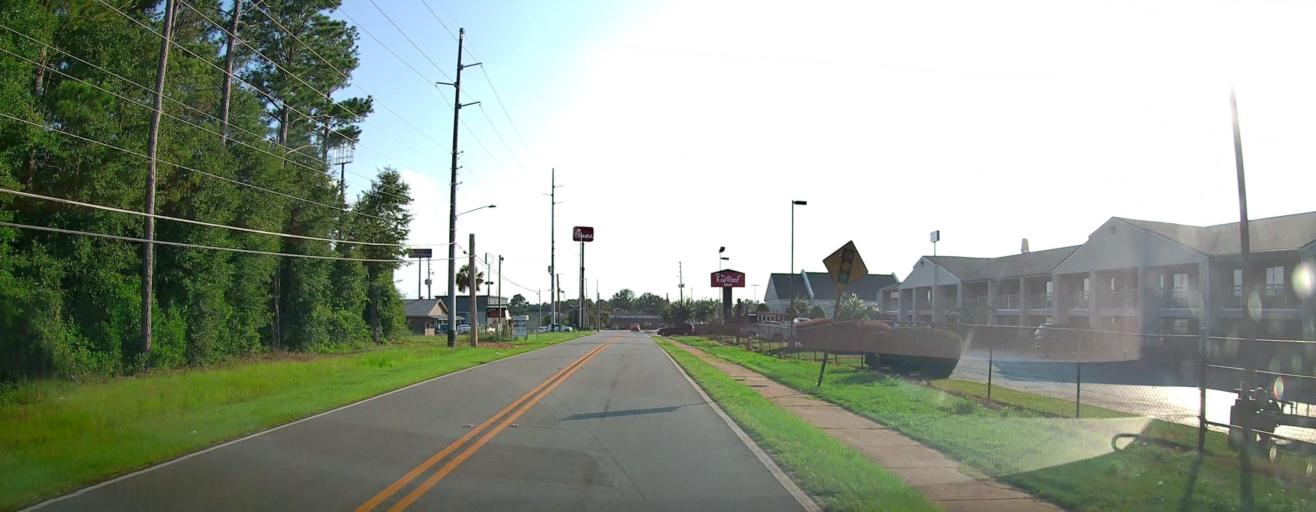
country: US
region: Georgia
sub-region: Houston County
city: Perry
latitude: 32.4689
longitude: -83.7385
